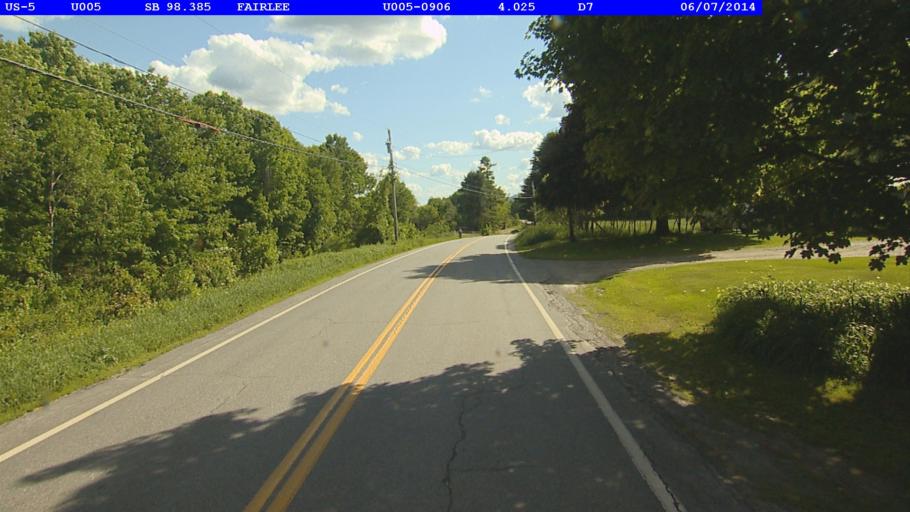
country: US
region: New Hampshire
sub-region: Grafton County
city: Orford
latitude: 43.9166
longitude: -72.1298
